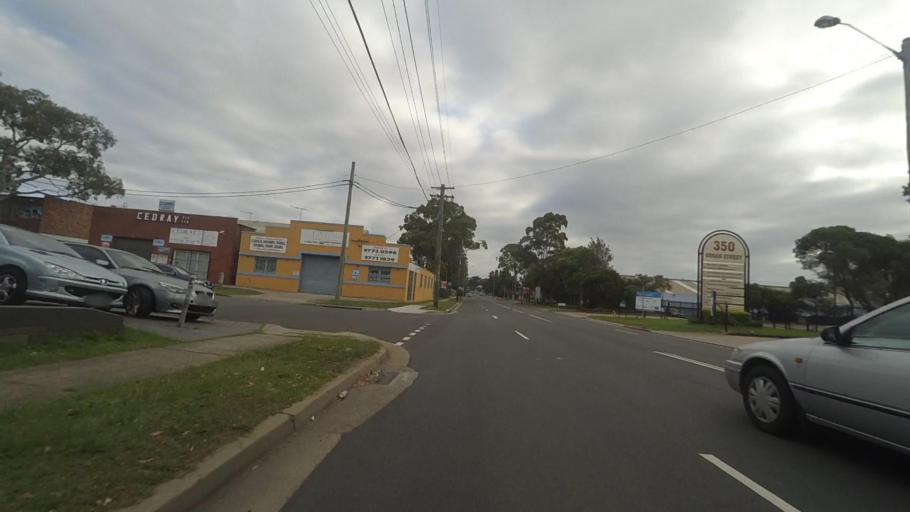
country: AU
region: New South Wales
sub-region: Bankstown
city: Revesby
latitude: -33.9325
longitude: 151.0120
